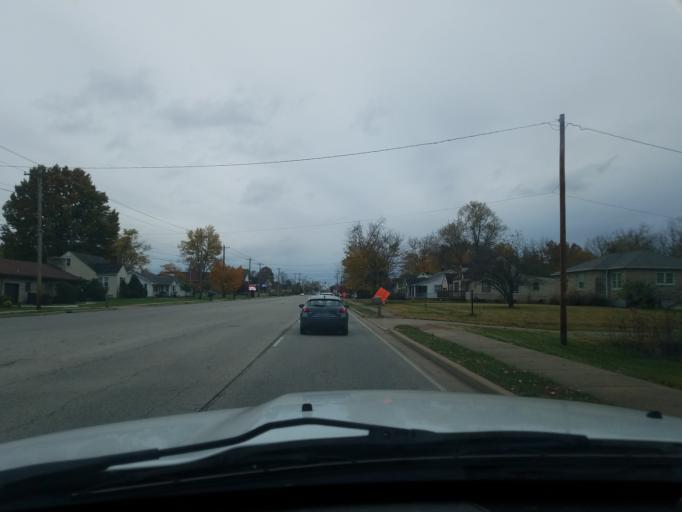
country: US
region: Indiana
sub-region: Floyd County
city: New Albany
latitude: 38.3282
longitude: -85.8001
